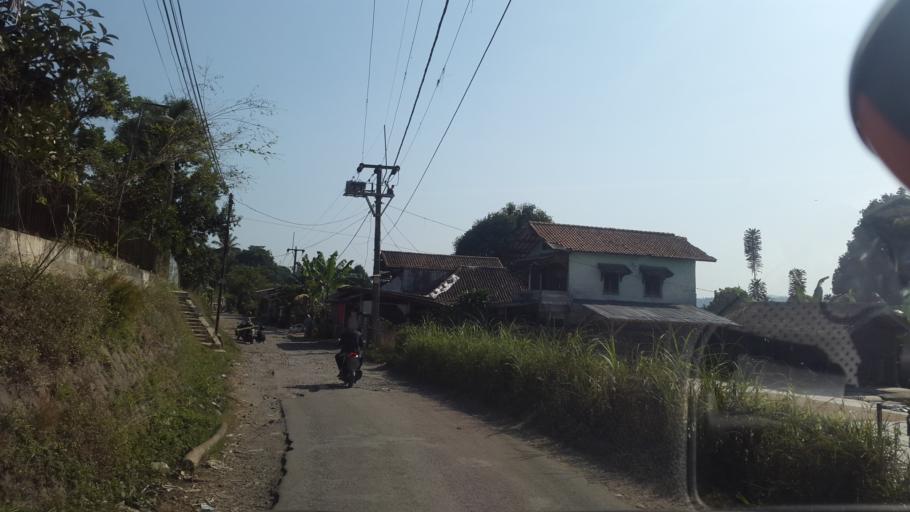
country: ID
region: West Java
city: Cicurug
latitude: -6.8594
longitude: 106.8024
